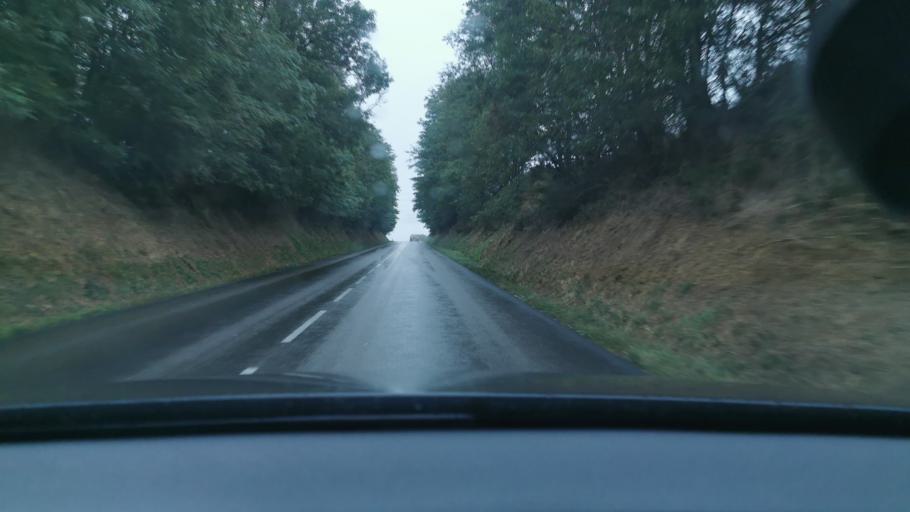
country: FR
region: Rhone-Alpes
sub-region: Departement du Rhone
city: Montanay
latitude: 45.8890
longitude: 4.8823
